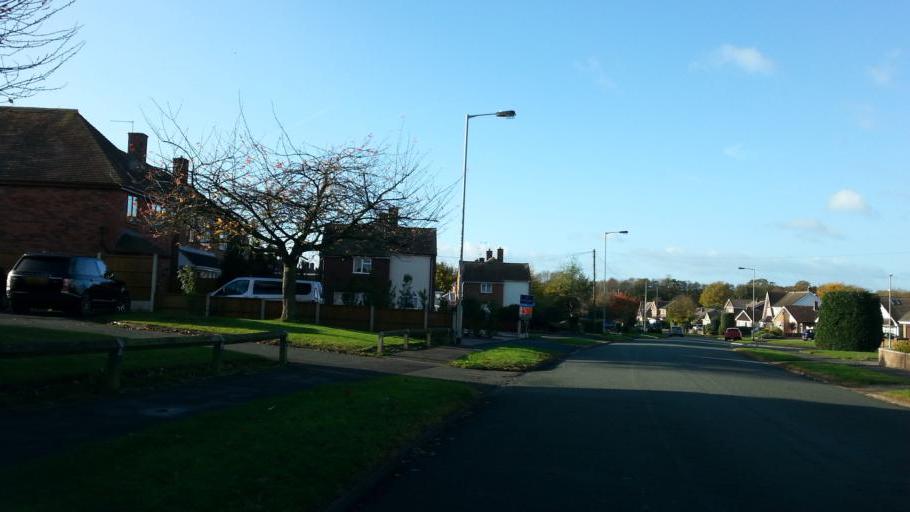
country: GB
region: England
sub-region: Staffordshire
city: Cannock
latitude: 52.6867
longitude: -2.0467
